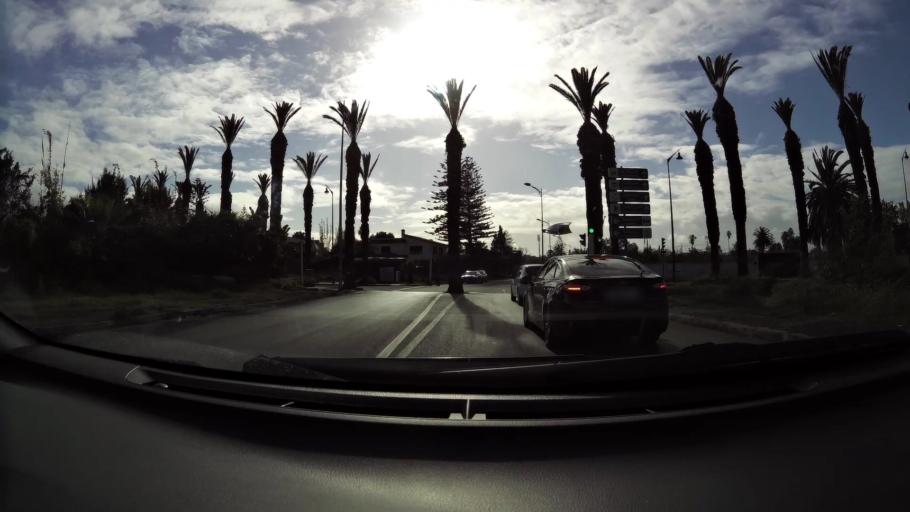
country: MA
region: Grand Casablanca
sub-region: Mohammedia
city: Mohammedia
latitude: 33.7026
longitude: -7.3867
